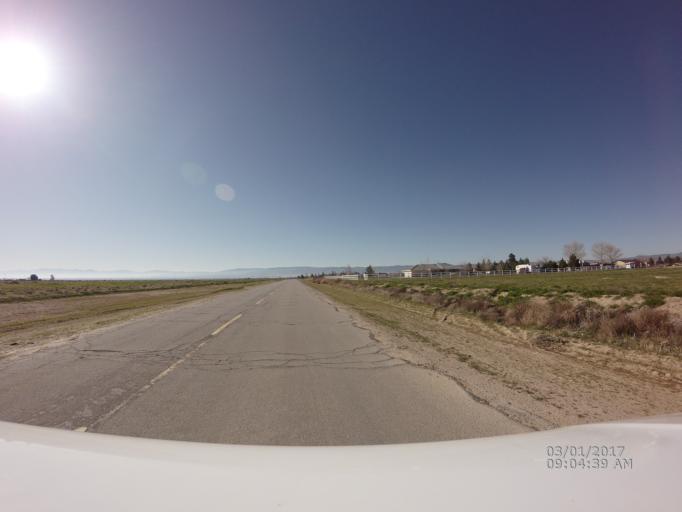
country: US
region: California
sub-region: Los Angeles County
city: Quartz Hill
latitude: 34.7688
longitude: -118.2725
